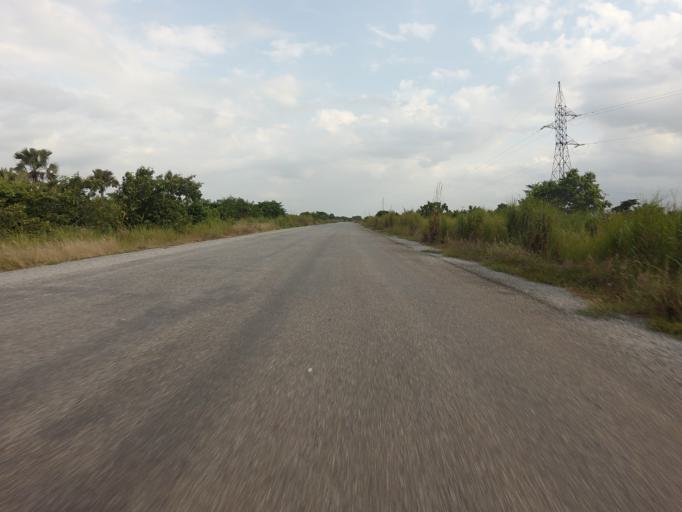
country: GH
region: Volta
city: Ho
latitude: 6.4029
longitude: 0.5245
